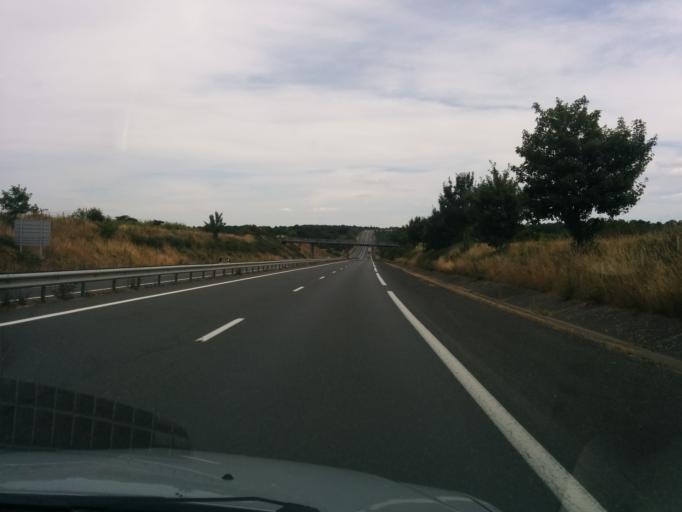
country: FR
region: Poitou-Charentes
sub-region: Departement des Deux-Sevres
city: Bressuire
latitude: 46.8584
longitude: -0.4993
